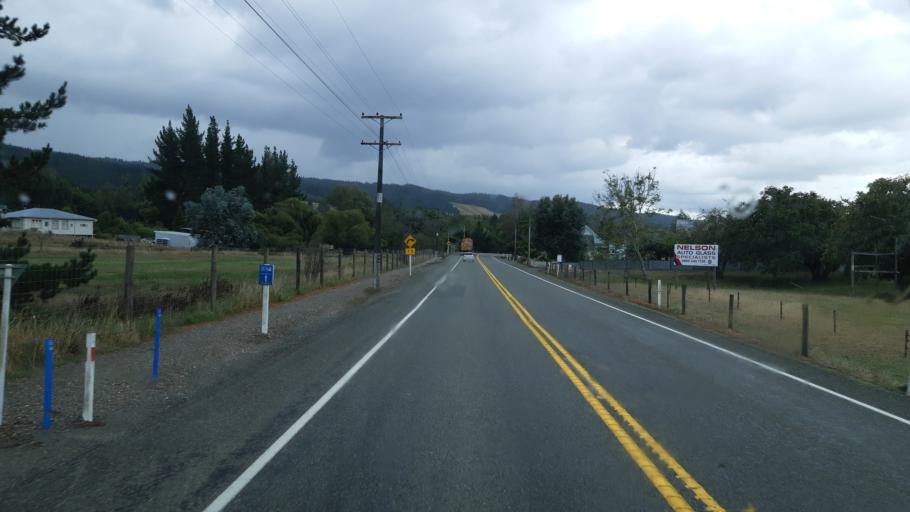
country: NZ
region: Tasman
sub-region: Tasman District
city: Wakefield
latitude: -41.4530
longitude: 172.9573
